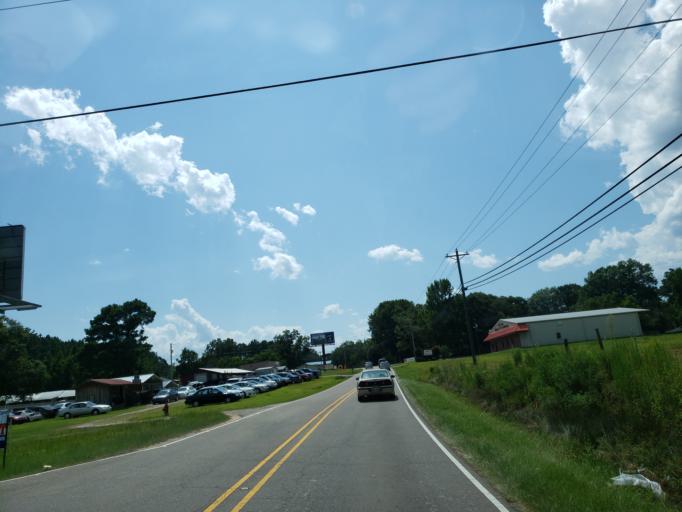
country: US
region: Mississippi
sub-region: Lamar County
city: West Hattiesburg
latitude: 31.2985
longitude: -89.3801
